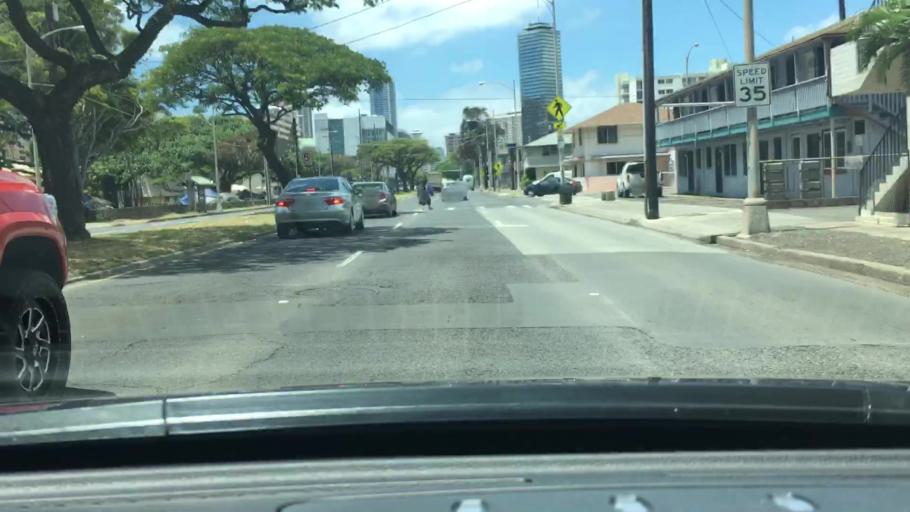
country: US
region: Hawaii
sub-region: Honolulu County
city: Honolulu
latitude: 21.2885
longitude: -157.8295
